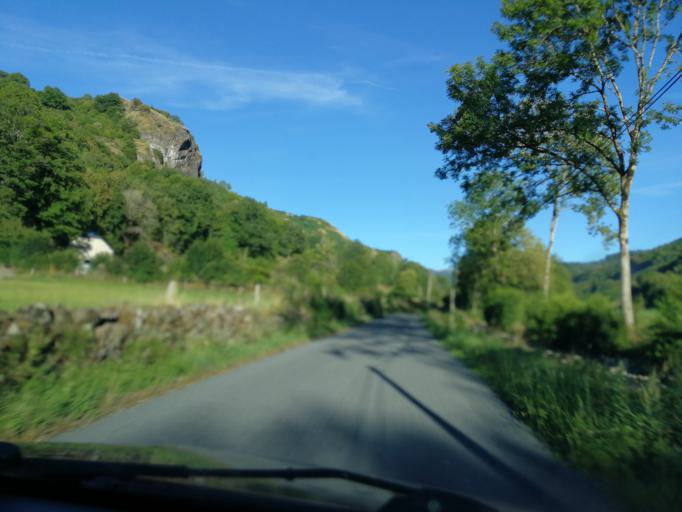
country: FR
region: Auvergne
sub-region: Departement du Cantal
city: Saint-Cernin
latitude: 45.1078
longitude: 2.5157
